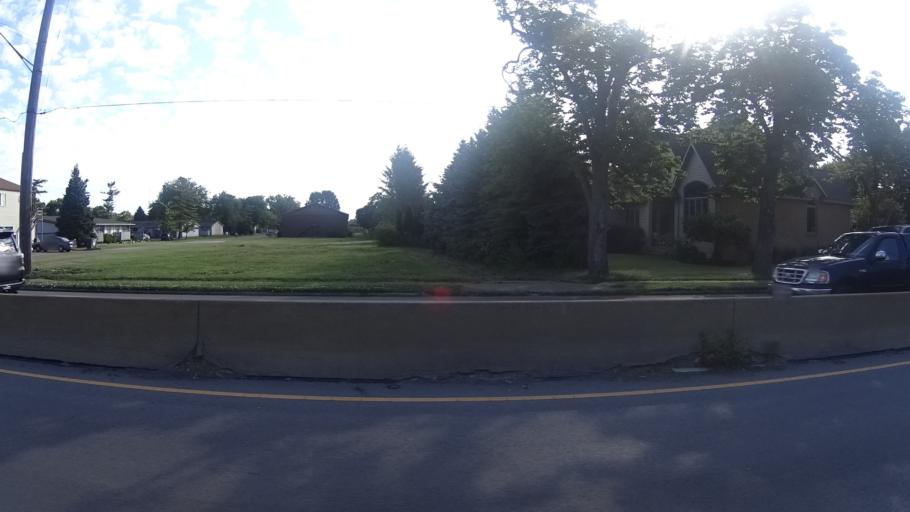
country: US
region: Ohio
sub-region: Erie County
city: Sandusky
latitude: 41.4354
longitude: -82.6910
